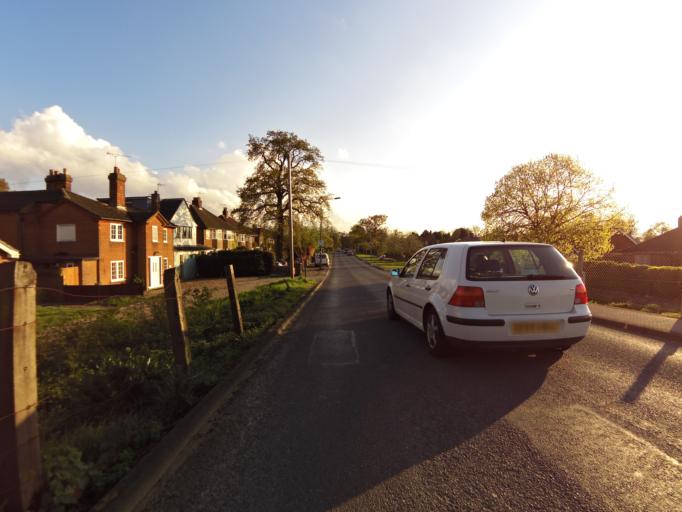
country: GB
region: England
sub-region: Suffolk
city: Ipswich
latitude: 52.0739
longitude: 1.1763
